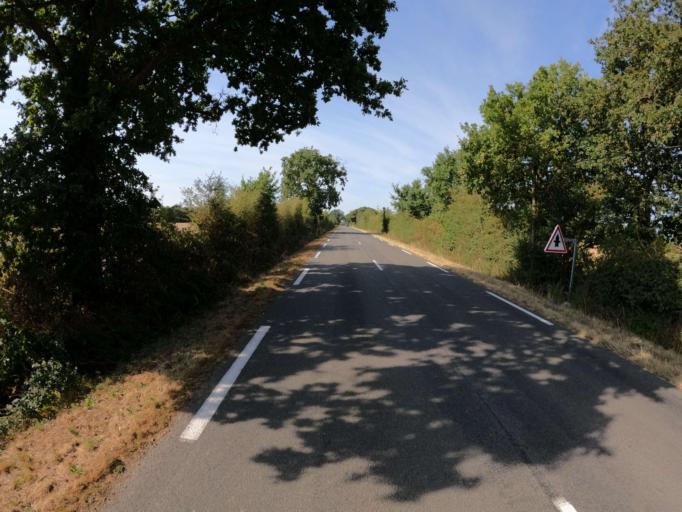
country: FR
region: Pays de la Loire
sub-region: Departement de la Vendee
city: Falleron
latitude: 46.8616
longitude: -1.7114
